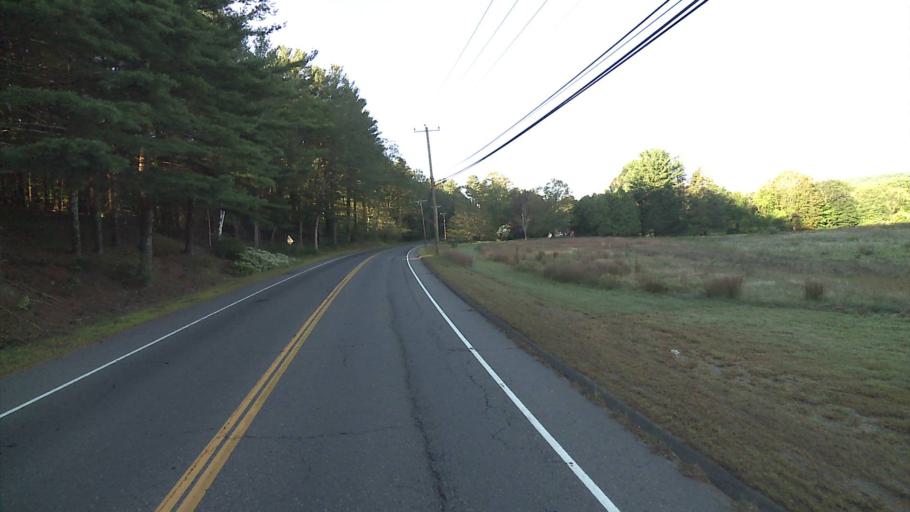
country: US
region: Connecticut
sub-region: Tolland County
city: Stafford Springs
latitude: 41.8905
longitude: -72.2921
